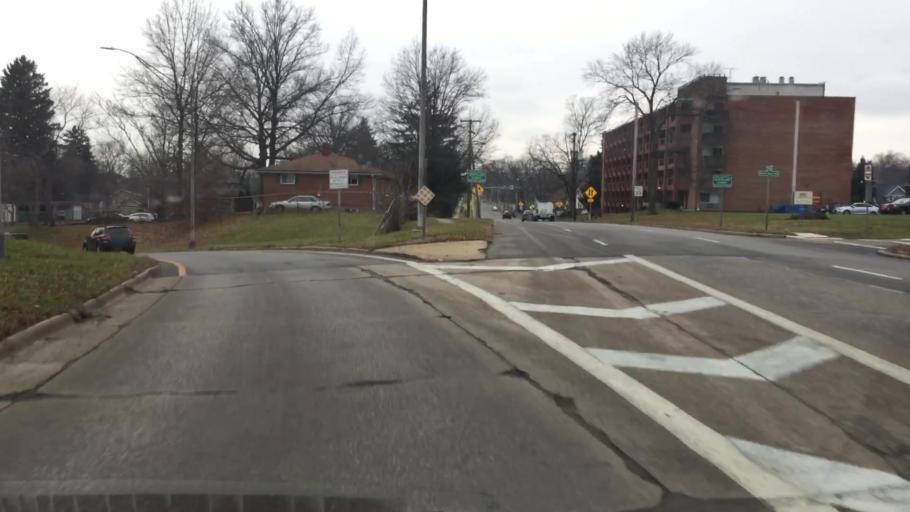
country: US
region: Ohio
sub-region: Summit County
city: Cuyahoga Falls
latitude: 41.1444
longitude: -81.4769
